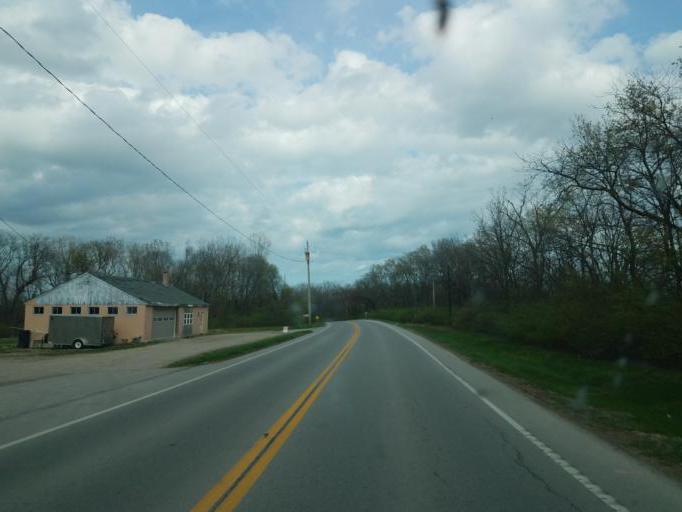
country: US
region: Ohio
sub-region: Erie County
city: Sandusky
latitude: 41.5336
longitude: -82.7641
